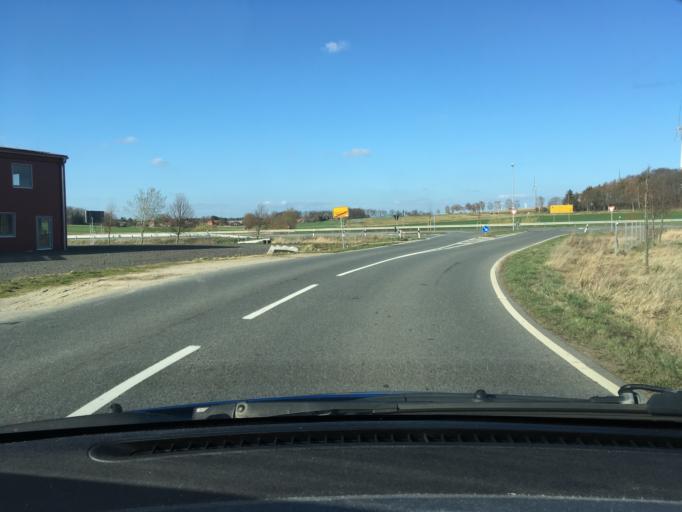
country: DE
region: Lower Saxony
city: Dahlem
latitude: 53.1935
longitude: 10.7477
